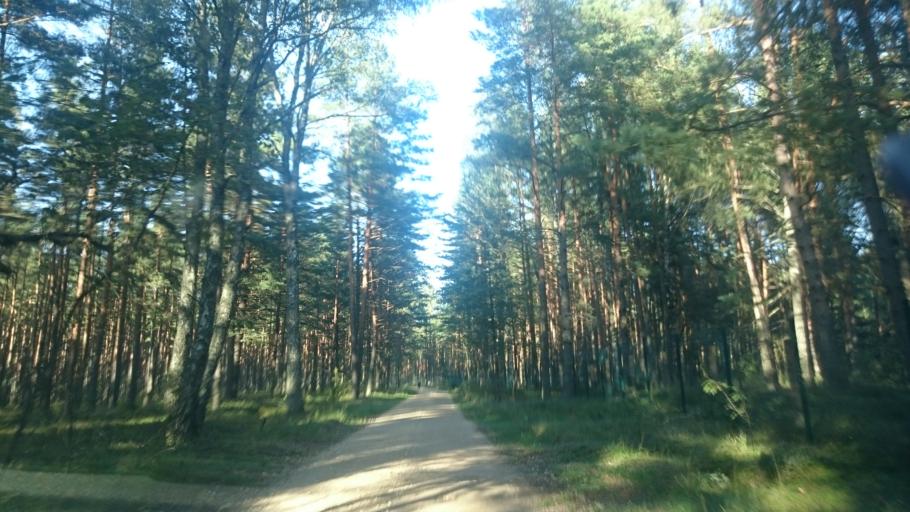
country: LV
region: Carnikava
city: Carnikava
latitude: 57.1047
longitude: 24.2324
